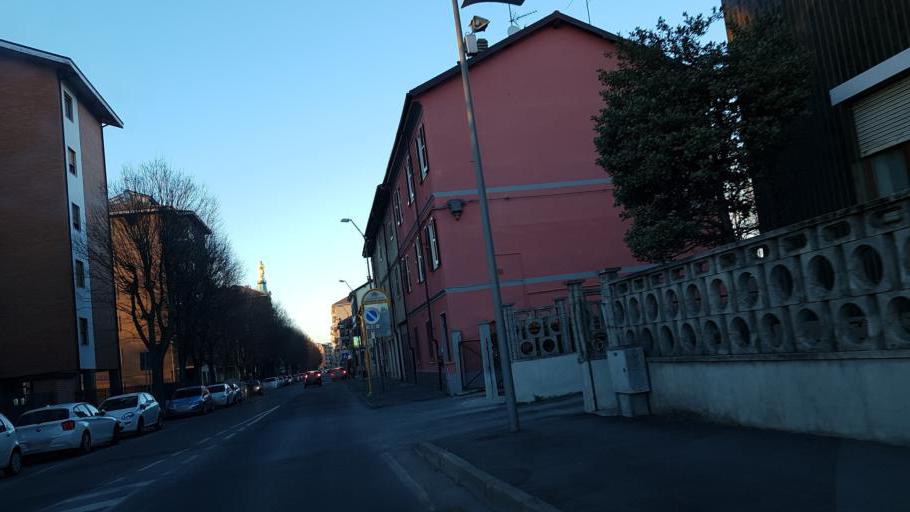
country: IT
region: Piedmont
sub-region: Provincia di Alessandria
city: Tortona
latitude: 44.8840
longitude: 8.8589
